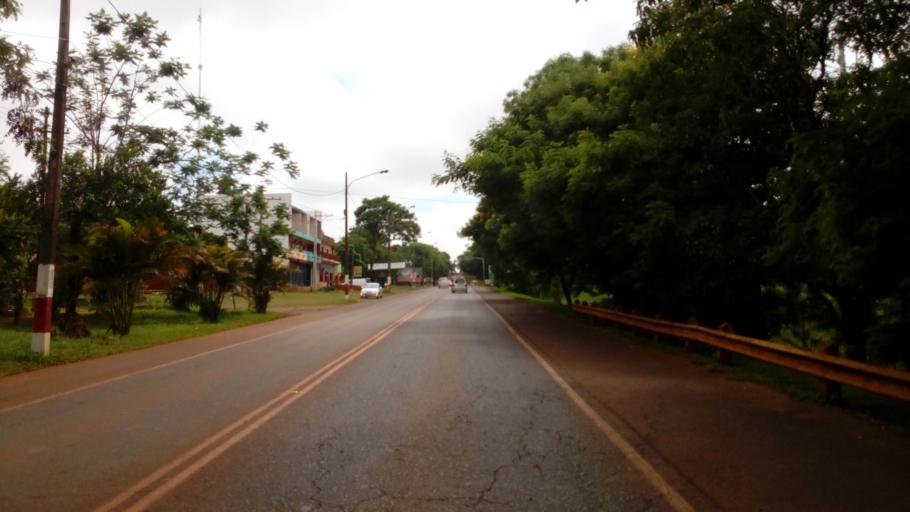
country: PY
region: Alto Parana
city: Ciudad del Este
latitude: -25.4106
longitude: -54.6334
